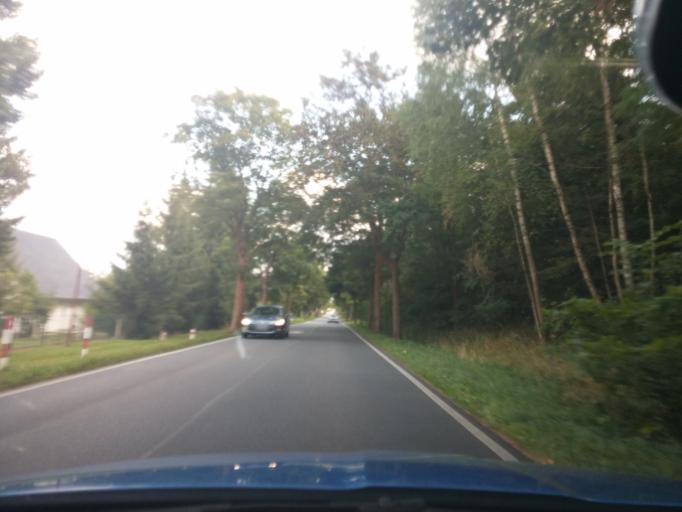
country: DE
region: Brandenburg
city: Halbe
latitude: 52.1095
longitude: 13.6873
